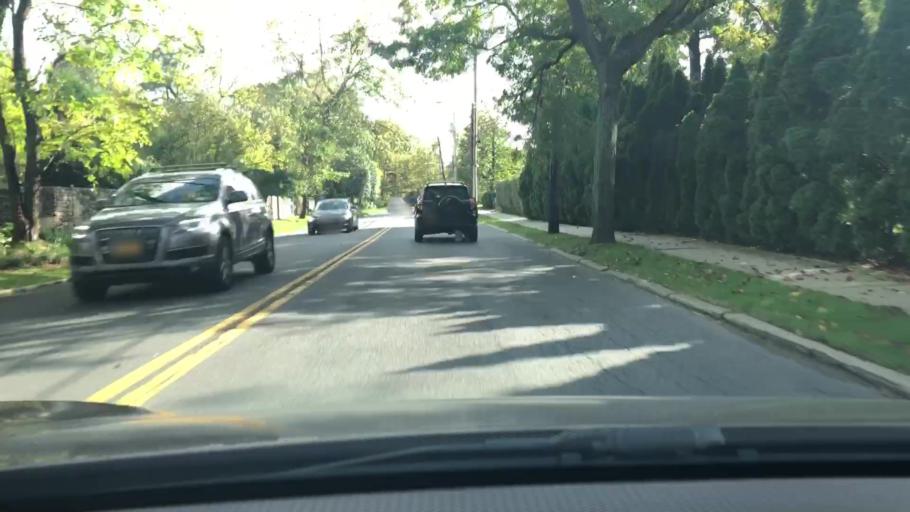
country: US
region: New York
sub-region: Westchester County
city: Tuckahoe
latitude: 40.9419
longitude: -73.8206
